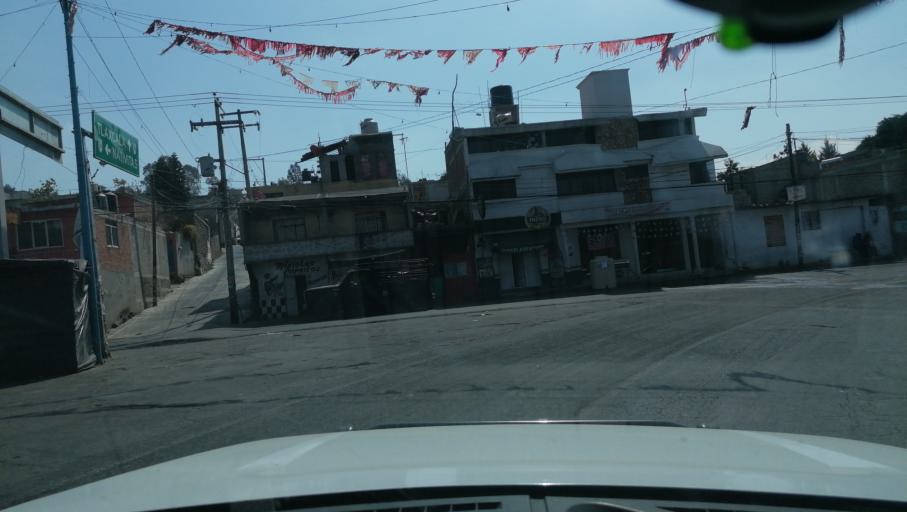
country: MX
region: Tlaxcala
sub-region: Tetlatlahuca
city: Tetlatlahuca
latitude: 19.2385
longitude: -98.3002
